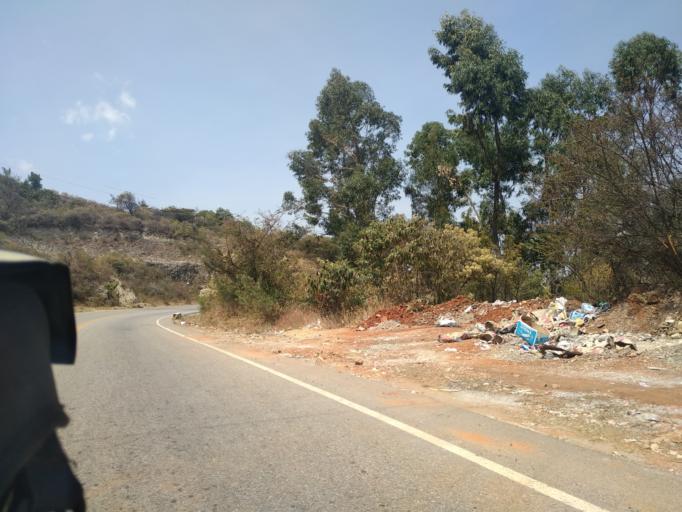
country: PE
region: Cajamarca
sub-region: Provincia de Cajabamba
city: Cauday
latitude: -7.6111
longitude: -78.0856
